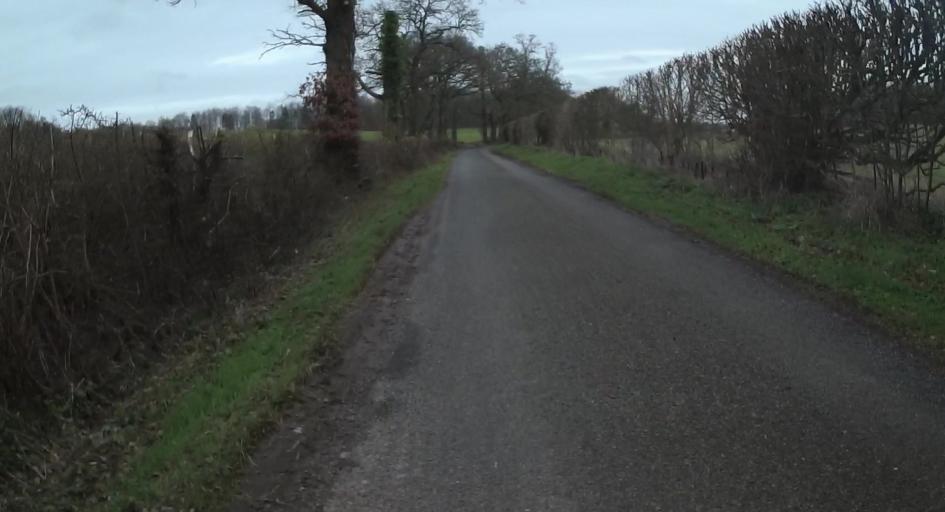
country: GB
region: England
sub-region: Hampshire
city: Overton
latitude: 51.2676
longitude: -1.2488
